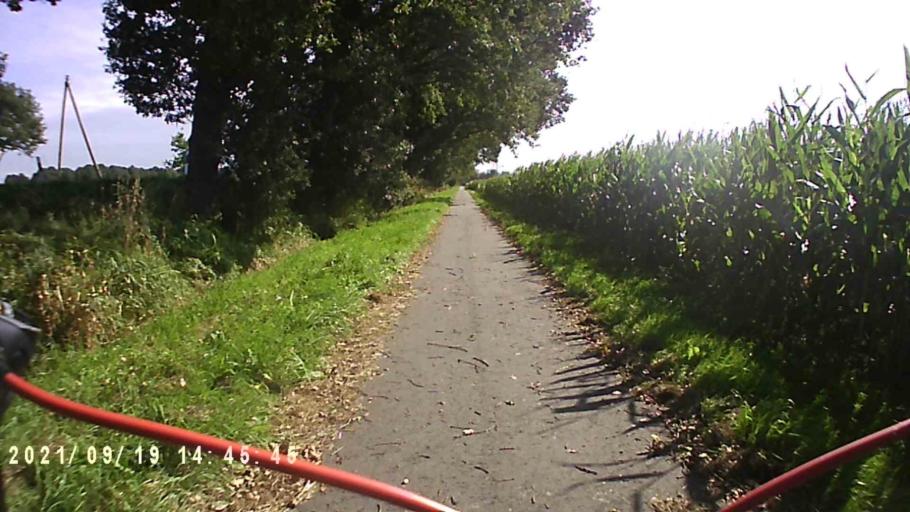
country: DE
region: Lower Saxony
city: Bunde
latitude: 53.1258
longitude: 7.1838
